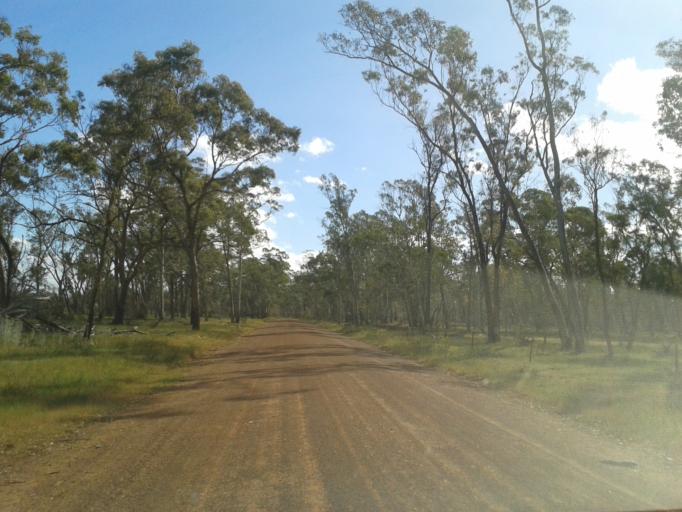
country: AU
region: Victoria
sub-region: Southern Grampians
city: Hamilton
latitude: -37.2458
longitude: 142.2003
